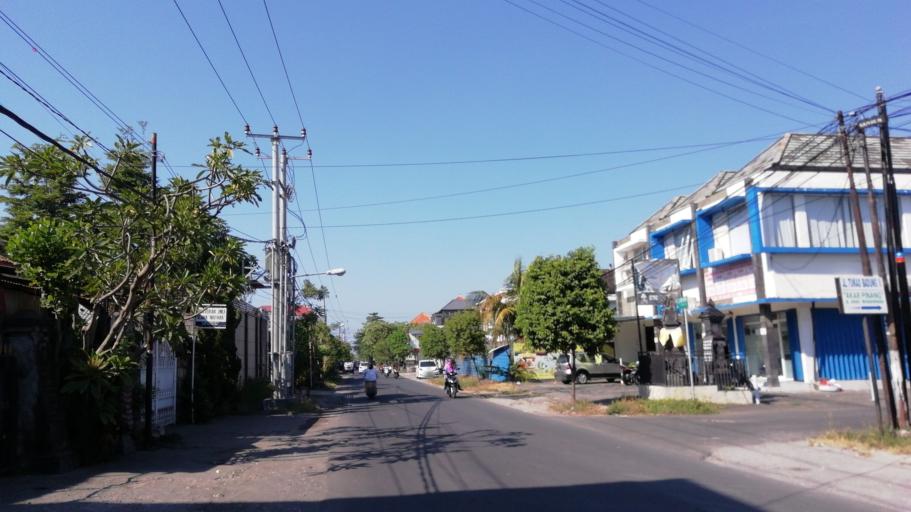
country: ID
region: Bali
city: Banjar Taman
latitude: -8.6786
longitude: 115.2378
